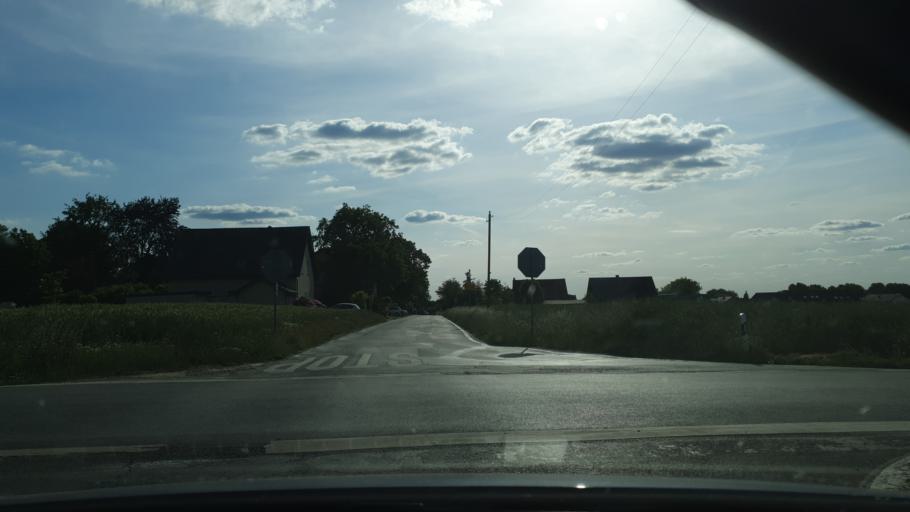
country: DE
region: North Rhine-Westphalia
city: Spenge
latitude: 52.1549
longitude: 8.5206
